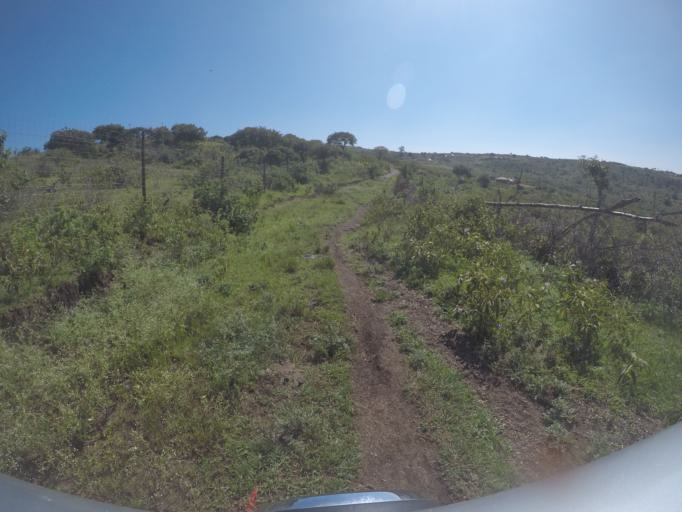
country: ZA
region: KwaZulu-Natal
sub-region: uThungulu District Municipality
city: Empangeni
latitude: -28.5608
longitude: 31.7031
